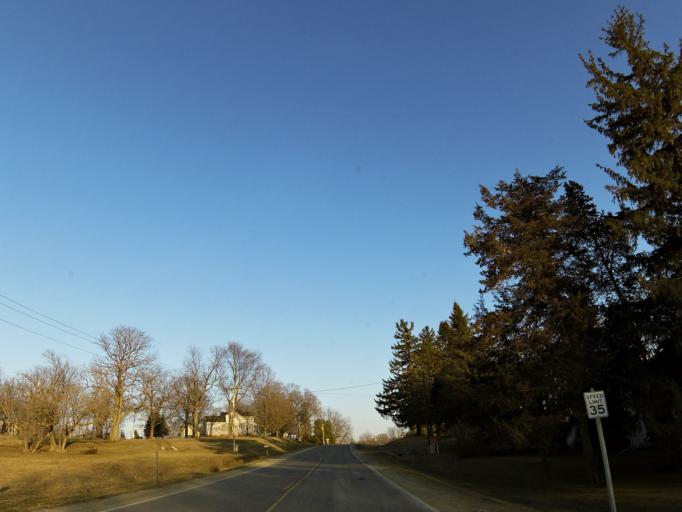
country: US
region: Iowa
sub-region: Mitchell County
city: Saint Ansgar
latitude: 43.3836
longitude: -92.9298
